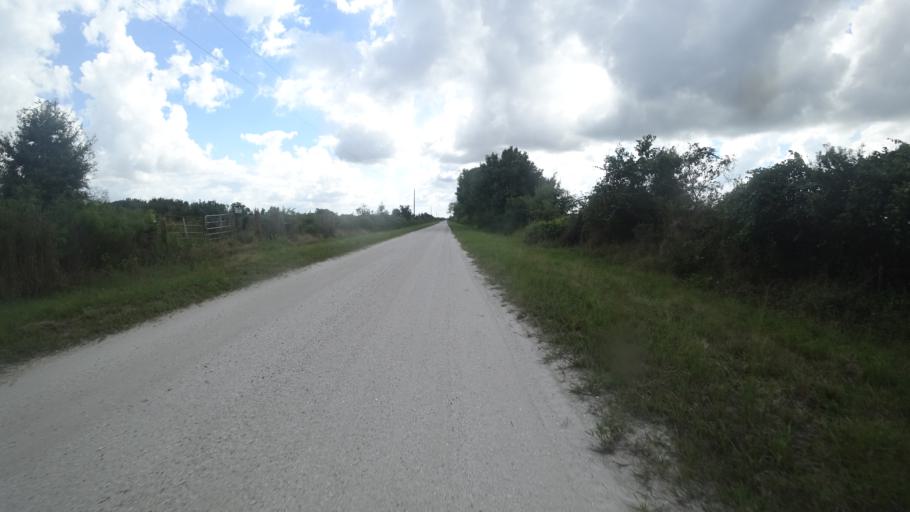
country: US
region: Florida
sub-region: Hillsborough County
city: Wimauma
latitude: 27.5718
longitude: -82.1741
